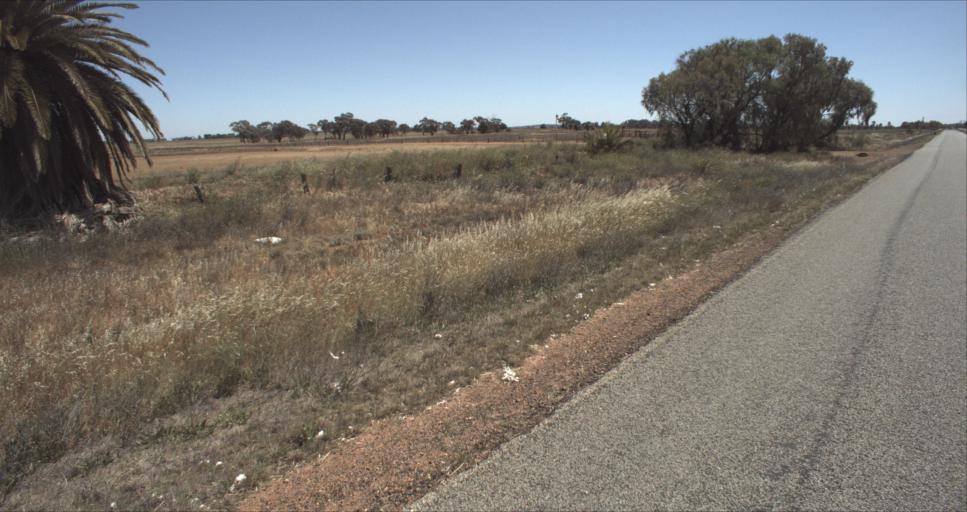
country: AU
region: New South Wales
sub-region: Leeton
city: Leeton
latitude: -34.4496
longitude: 146.2962
